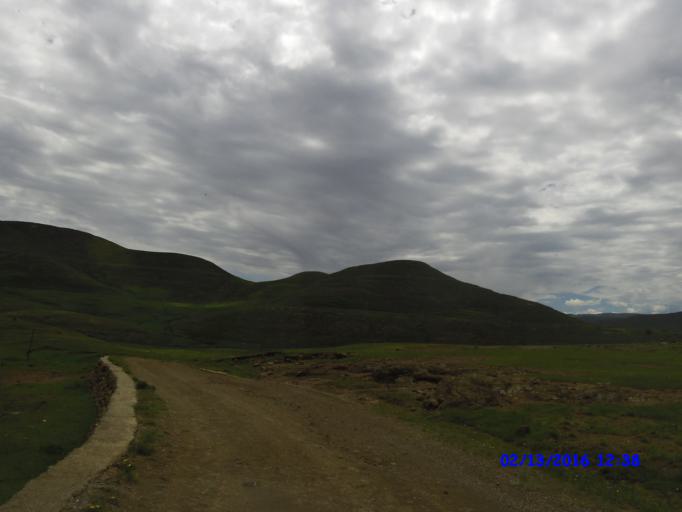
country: LS
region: Maseru
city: Nako
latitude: -29.8366
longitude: 28.0281
